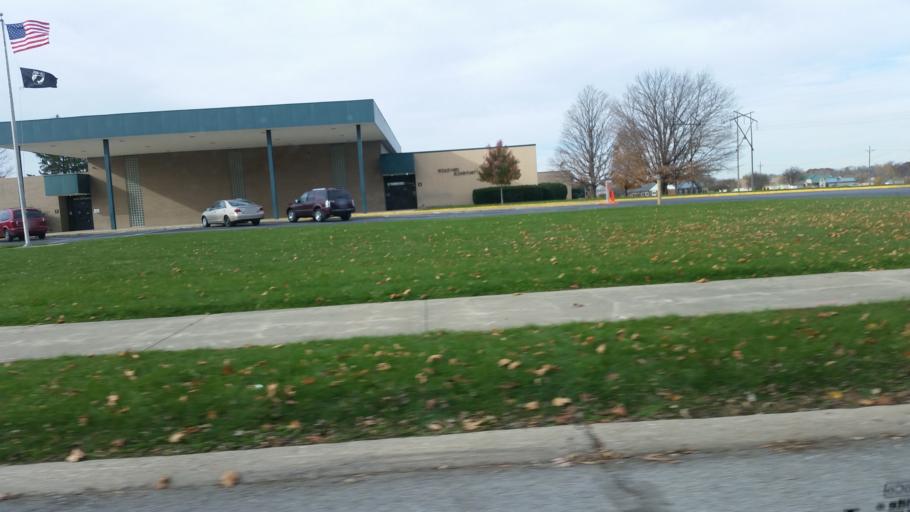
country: US
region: Indiana
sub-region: Howard County
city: Kokomo
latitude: 40.4609
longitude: -86.1556
